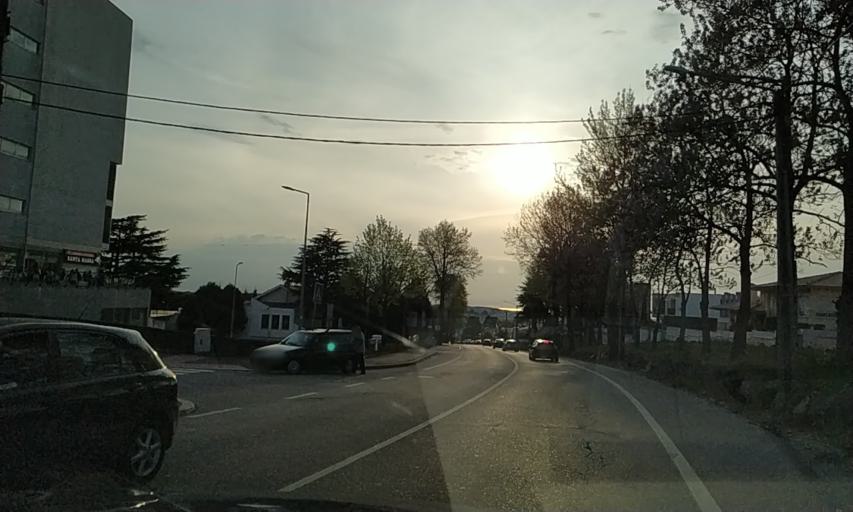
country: PT
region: Porto
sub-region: Gondomar
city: Baguim do Monte
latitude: 41.2072
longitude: -8.5327
